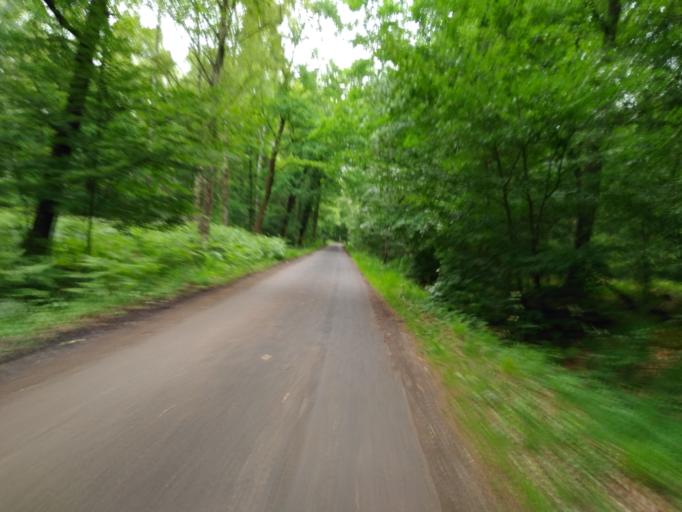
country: DE
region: North Rhine-Westphalia
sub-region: Regierungsbezirk Dusseldorf
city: Schermbeck
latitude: 51.6490
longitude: 6.8400
